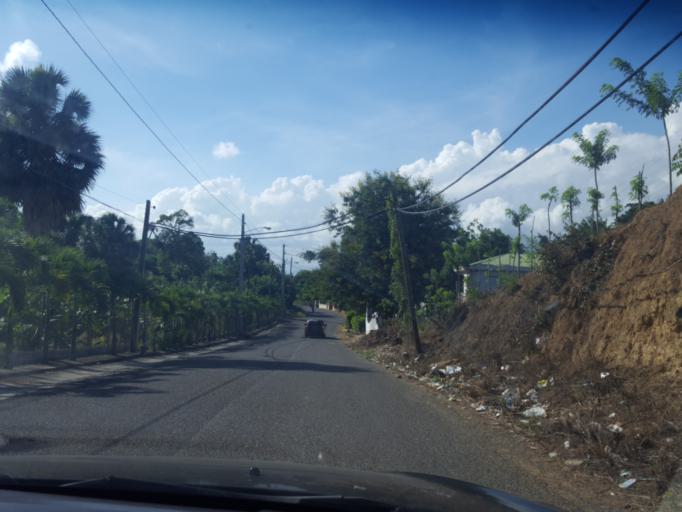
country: DO
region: La Vega
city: Rio Verde Arriba
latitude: 19.3507
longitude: -70.6026
